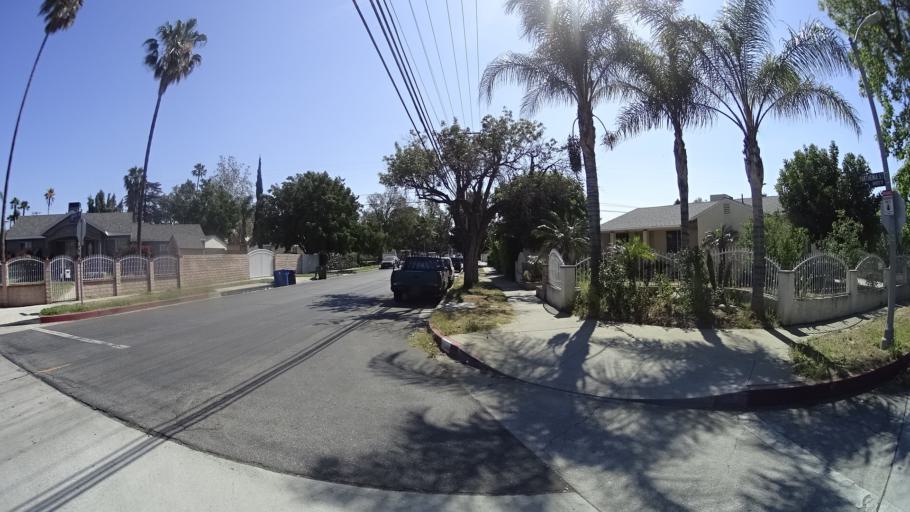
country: US
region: California
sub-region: Los Angeles County
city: Van Nuys
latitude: 34.2289
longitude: -118.4470
